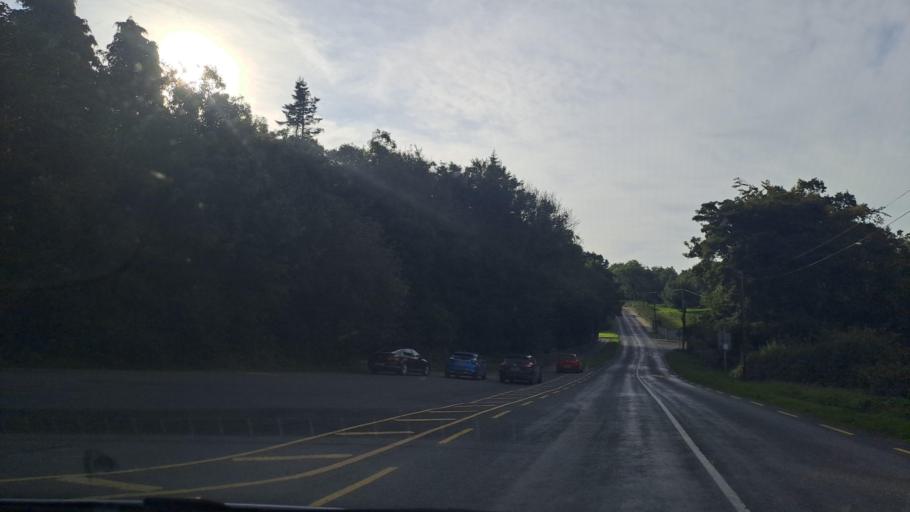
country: IE
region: Ulster
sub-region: An Cabhan
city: Kingscourt
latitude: 53.9198
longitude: -6.8119
